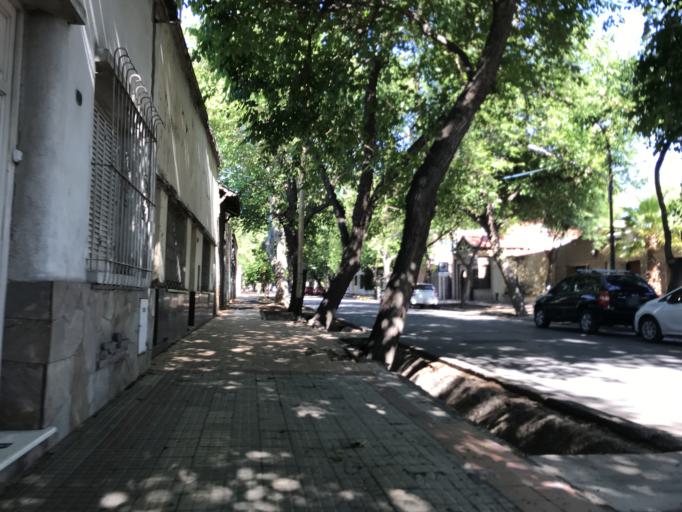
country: AR
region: Mendoza
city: Mendoza
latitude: -32.8766
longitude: -68.8313
